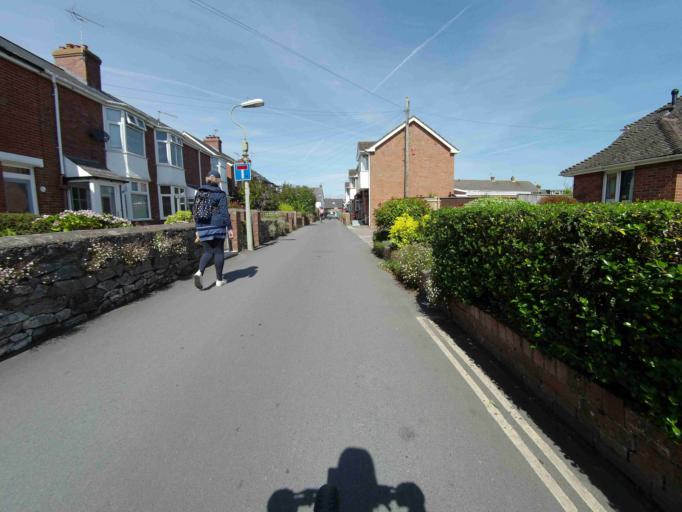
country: GB
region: England
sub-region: Devon
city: Topsham
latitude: 50.6870
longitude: -3.4695
